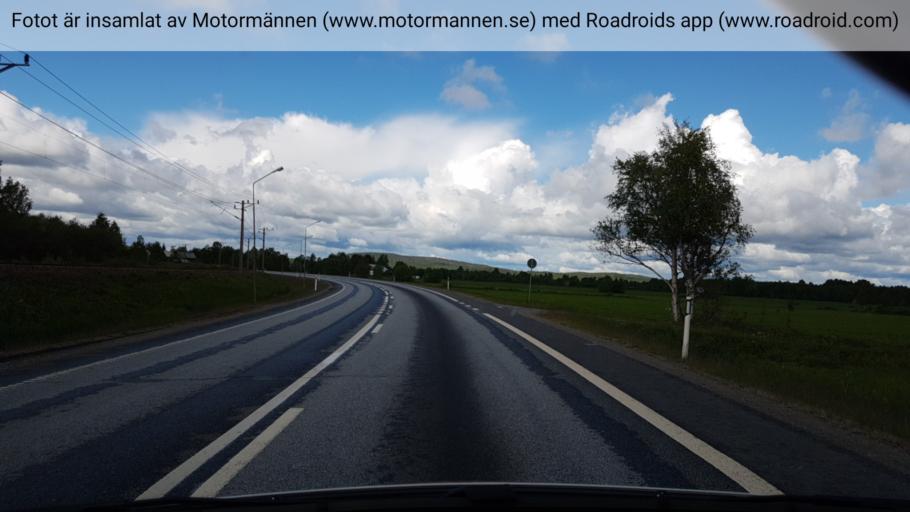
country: SE
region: Vaesterbotten
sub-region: Vannas Kommun
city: Vannasby
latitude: 63.9204
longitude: 19.8696
